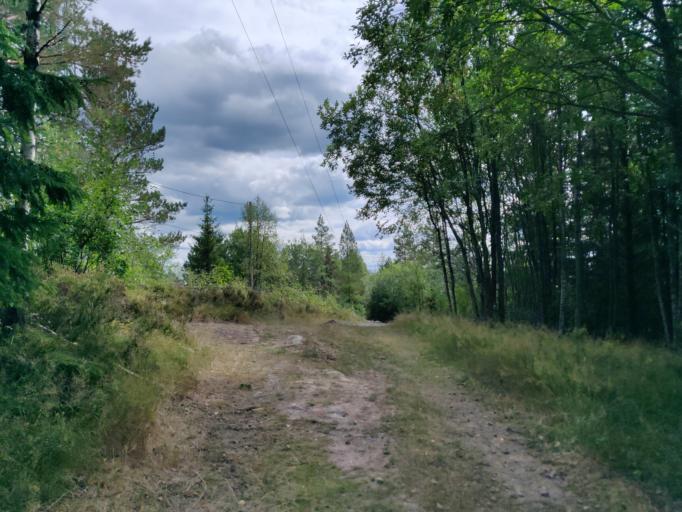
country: SE
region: Vaermland
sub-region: Hagfors Kommun
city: Hagfors
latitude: 60.0217
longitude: 13.7308
